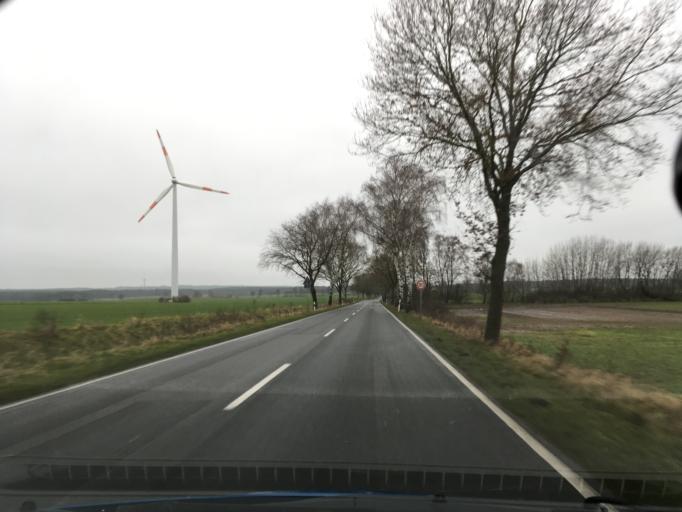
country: DE
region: Lower Saxony
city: Reinstorf
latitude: 53.2634
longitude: 10.5801
